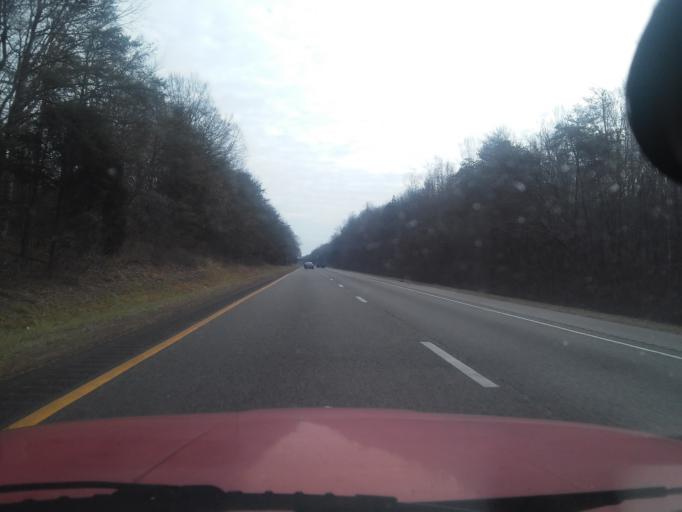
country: US
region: Virginia
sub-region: Goochland County
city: Goochland
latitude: 37.8096
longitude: -77.9332
